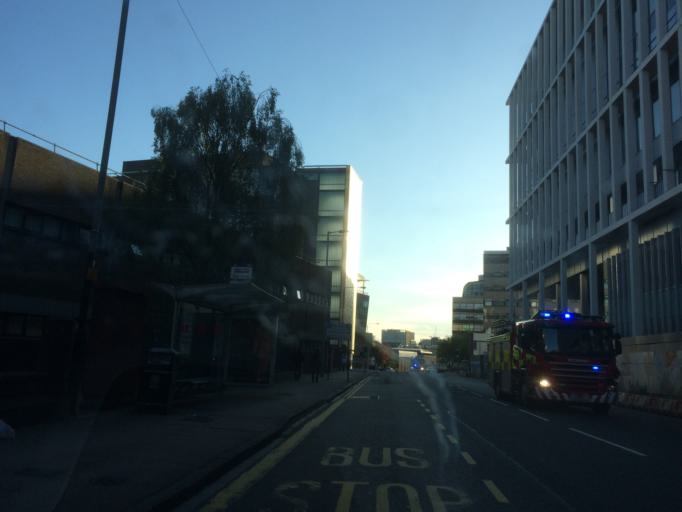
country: GB
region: Scotland
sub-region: Glasgow City
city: Glasgow
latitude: 55.8630
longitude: -4.2436
